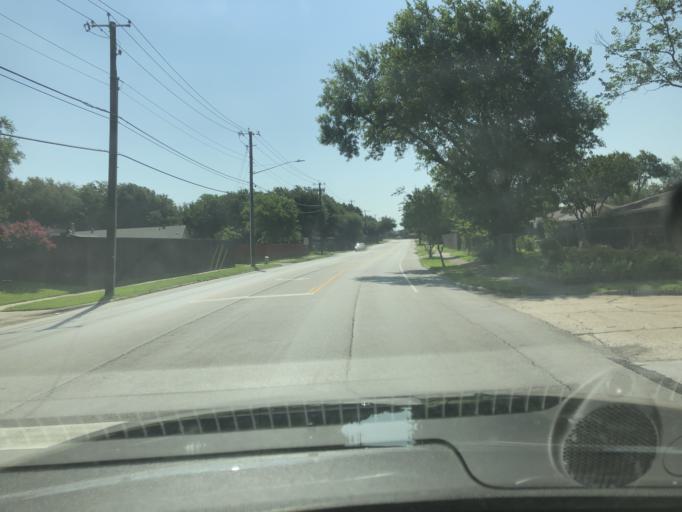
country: US
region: Texas
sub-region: Dallas County
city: Sunnyvale
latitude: 32.8368
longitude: -96.5921
